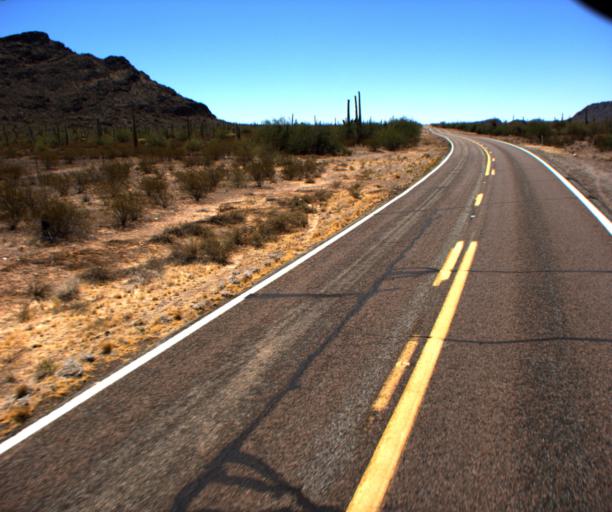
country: US
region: Arizona
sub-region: Pima County
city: Ajo
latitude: 32.2290
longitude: -112.7104
